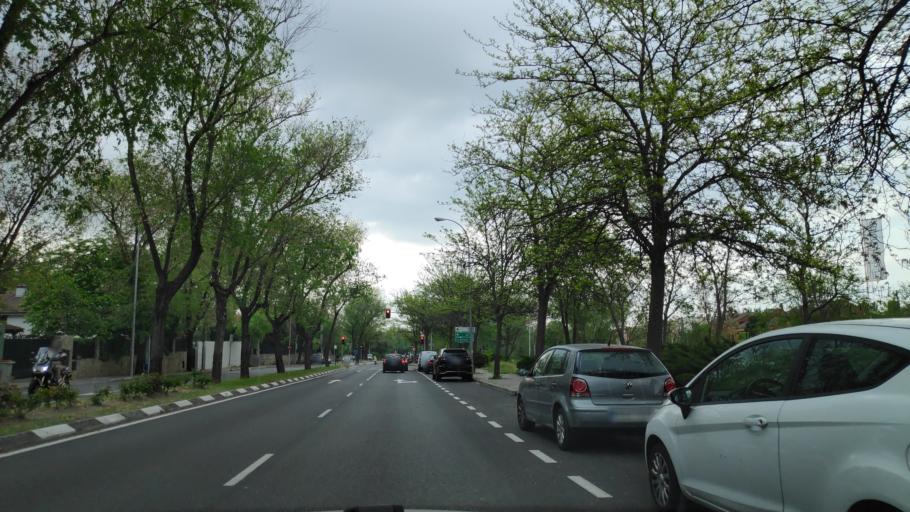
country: ES
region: Madrid
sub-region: Provincia de Madrid
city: Pozuelo de Alarcon
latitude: 40.4613
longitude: -3.7916
